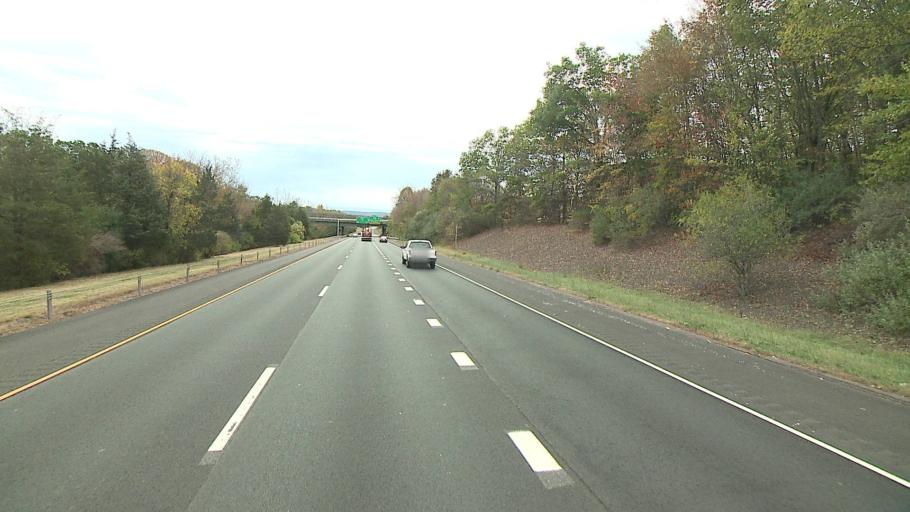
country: US
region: Connecticut
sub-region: Middlesex County
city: Cromwell
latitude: 41.6098
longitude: -72.6776
